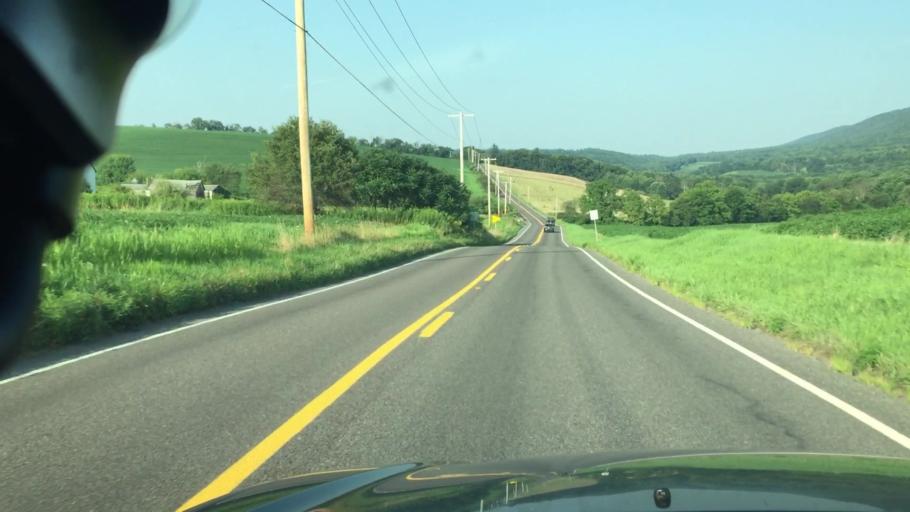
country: US
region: Pennsylvania
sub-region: Columbia County
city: Almedia
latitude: 40.9923
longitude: -76.3375
